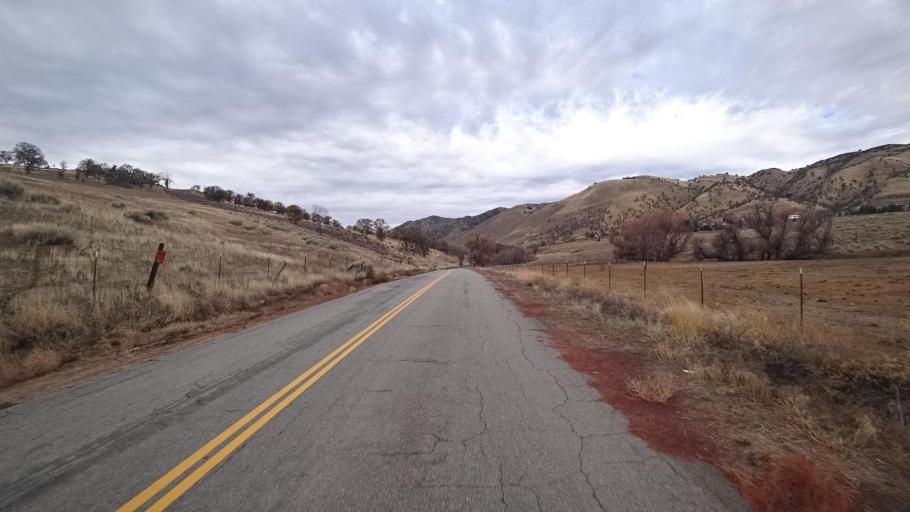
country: US
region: California
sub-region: Kern County
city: Golden Hills
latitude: 35.1235
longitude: -118.5535
